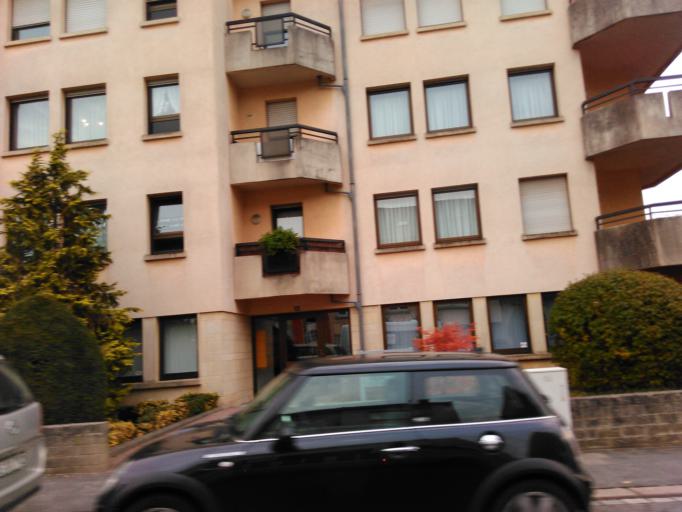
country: LU
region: Luxembourg
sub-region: Canton de Luxembourg
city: Luxembourg
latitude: 49.6184
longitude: 6.1185
